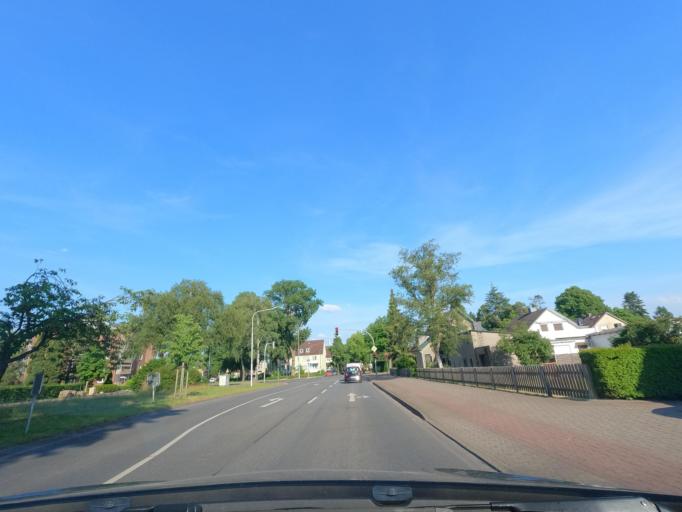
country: DE
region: Schleswig-Holstein
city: Uetersen
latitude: 53.6894
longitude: 9.6665
